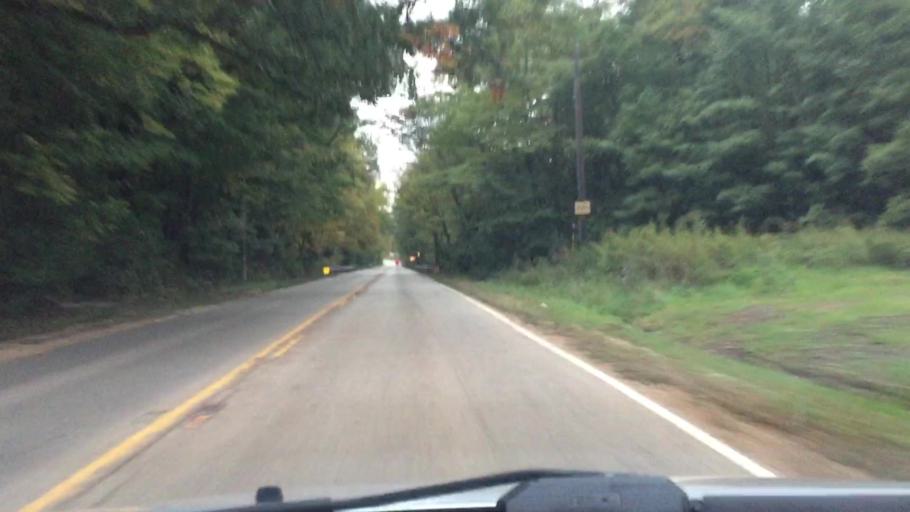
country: US
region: Illinois
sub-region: McHenry County
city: Algonquin
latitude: 42.1472
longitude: -88.2947
